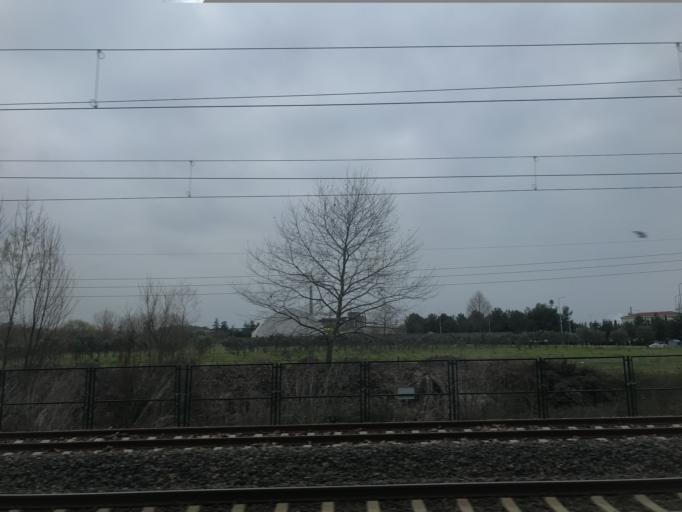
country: TR
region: Kocaeli
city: Darica
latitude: 40.8099
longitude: 29.3522
